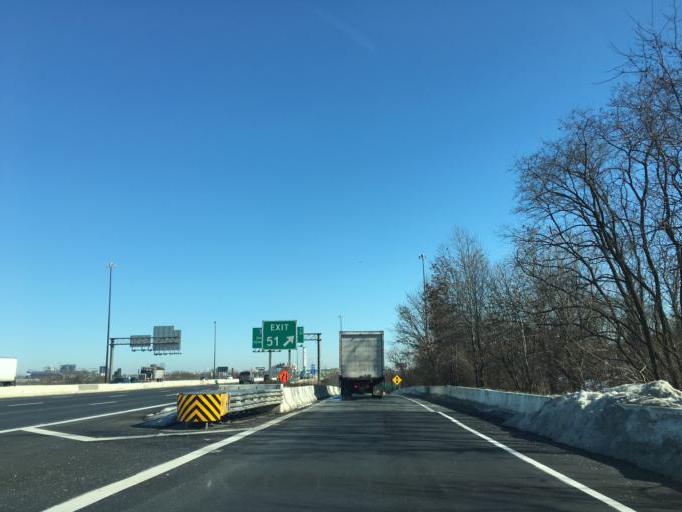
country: US
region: Maryland
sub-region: Baltimore County
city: Lansdowne
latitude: 39.2712
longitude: -76.6514
